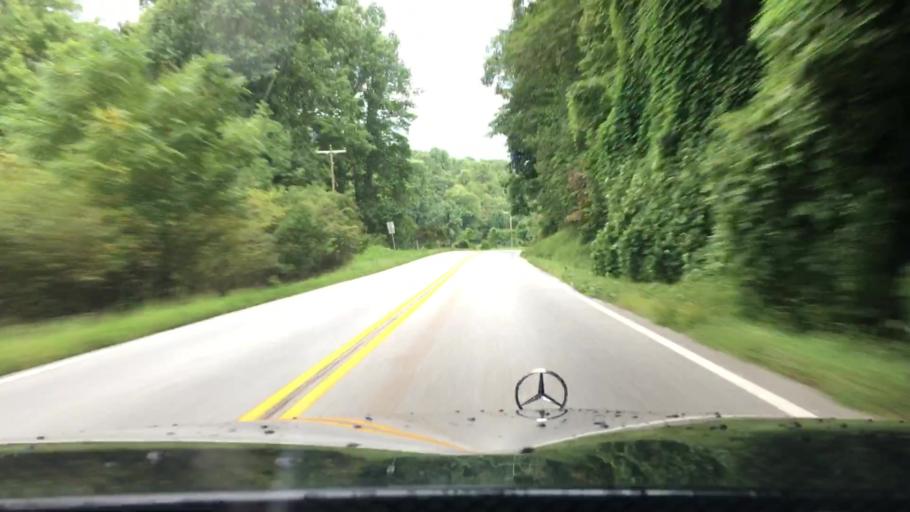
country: US
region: Virginia
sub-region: Nelson County
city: Nellysford
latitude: 37.8378
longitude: -78.9280
